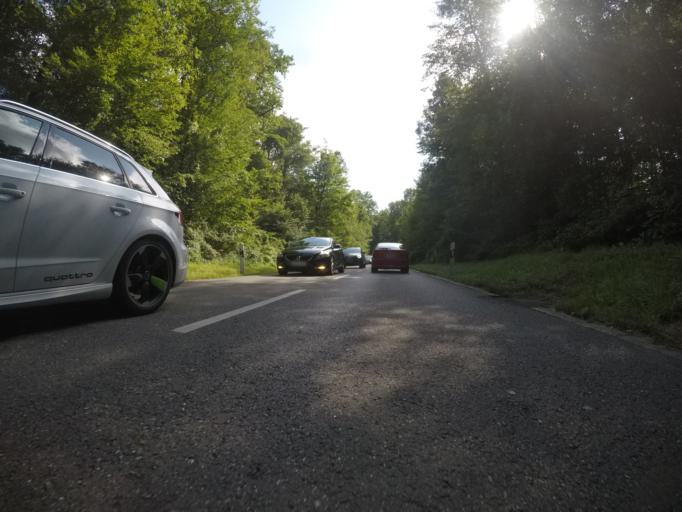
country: DE
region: Baden-Wuerttemberg
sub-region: Regierungsbezirk Stuttgart
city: Gerlingen
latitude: 48.7930
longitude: 9.0920
